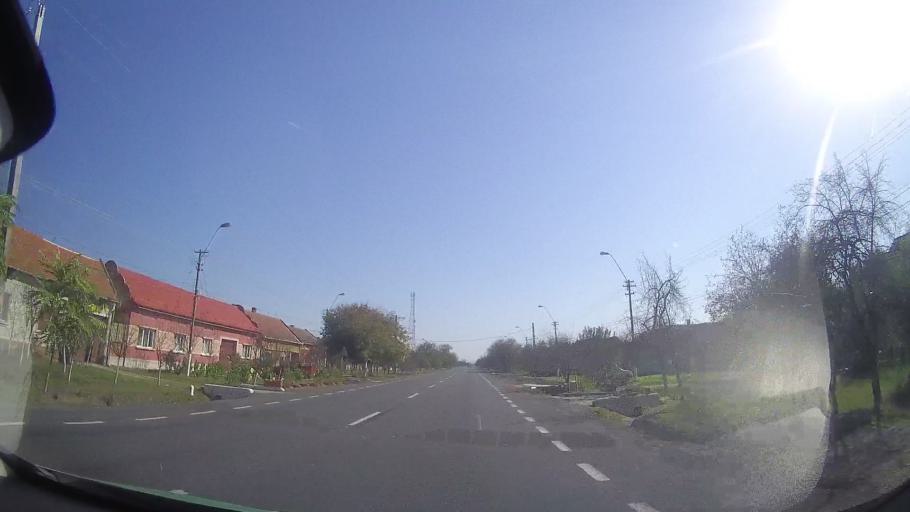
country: RO
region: Timis
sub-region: Comuna Belint
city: Belint
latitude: 45.7485
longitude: 21.7718
